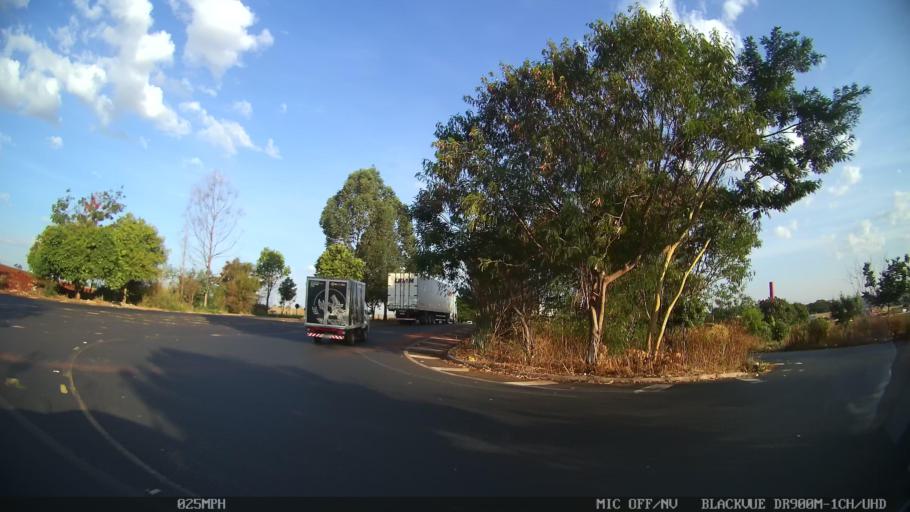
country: BR
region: Sao Paulo
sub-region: Ribeirao Preto
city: Ribeirao Preto
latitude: -21.2048
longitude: -47.7498
